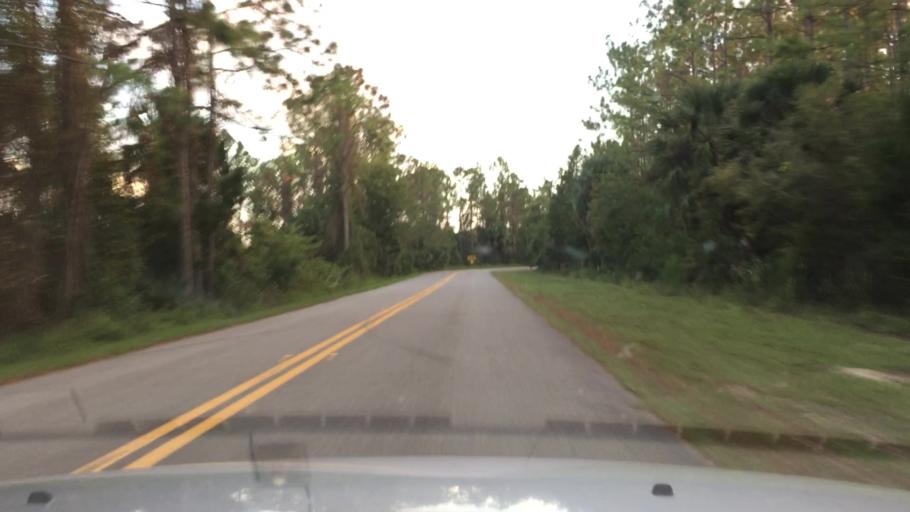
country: US
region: Florida
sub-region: Volusia County
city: Ormond Beach
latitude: 29.2837
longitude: -81.1236
